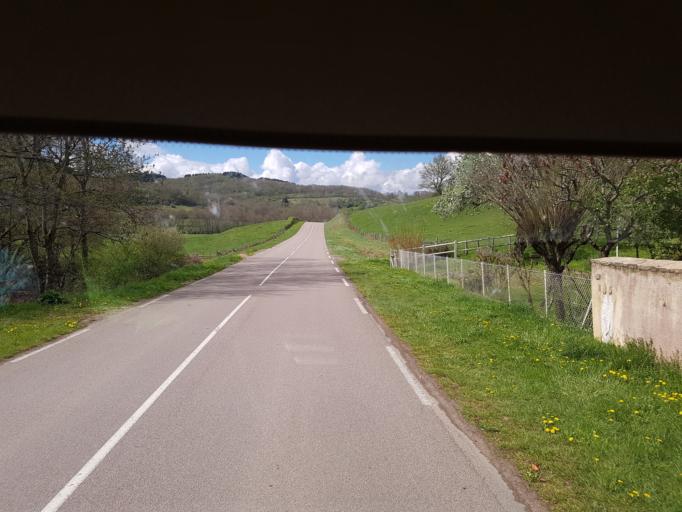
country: FR
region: Bourgogne
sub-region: Departement de Saone-et-Loire
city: Autun
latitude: 47.0956
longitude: 4.2344
